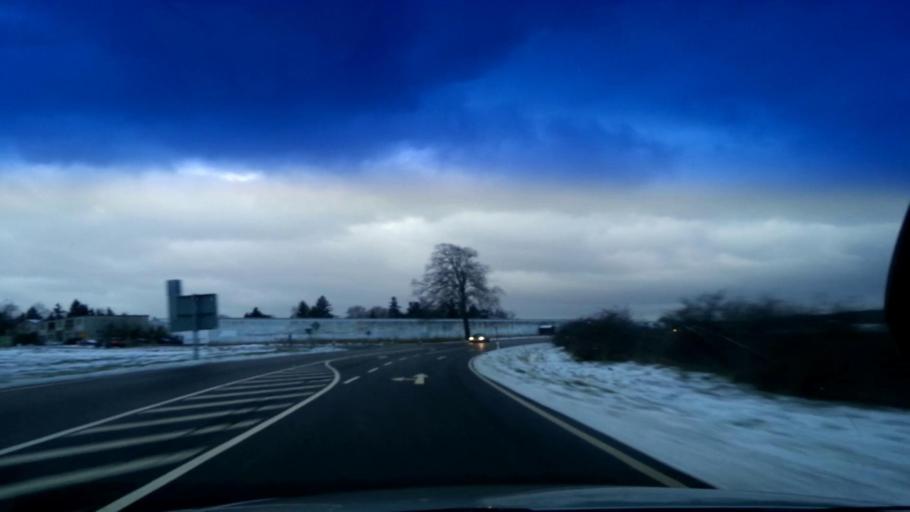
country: DE
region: Bavaria
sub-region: Upper Franconia
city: Marktleuthen
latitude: 50.1381
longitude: 12.0125
